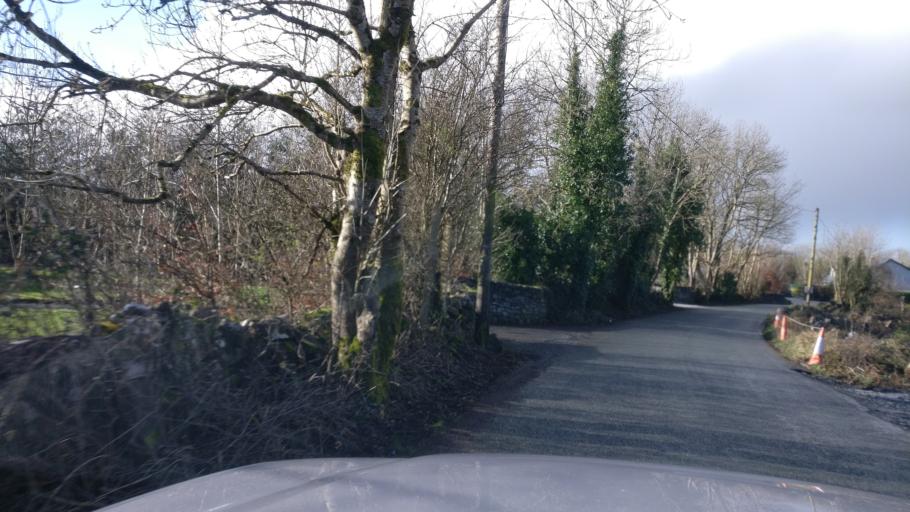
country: IE
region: Connaught
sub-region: County Galway
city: Athenry
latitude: 53.2377
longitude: -8.8157
